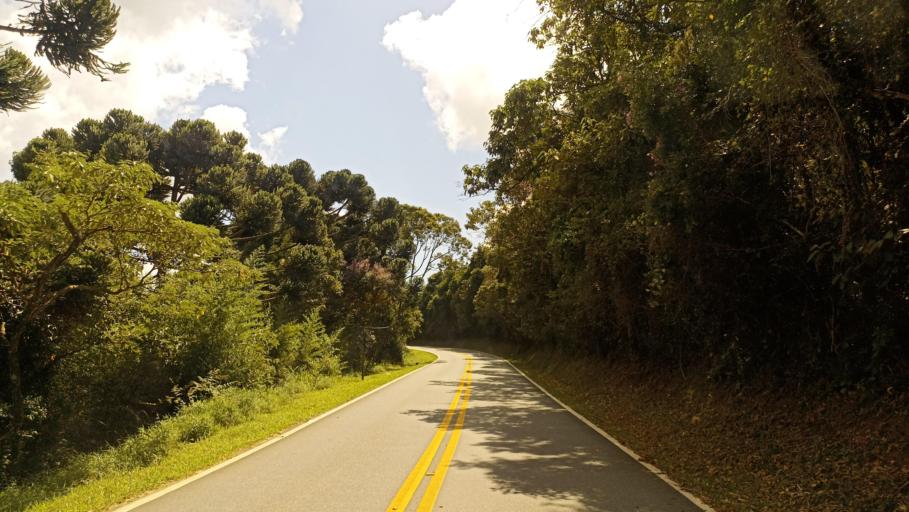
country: BR
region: Sao Paulo
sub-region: Cunha
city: Cunha
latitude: -23.1477
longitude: -44.8883
